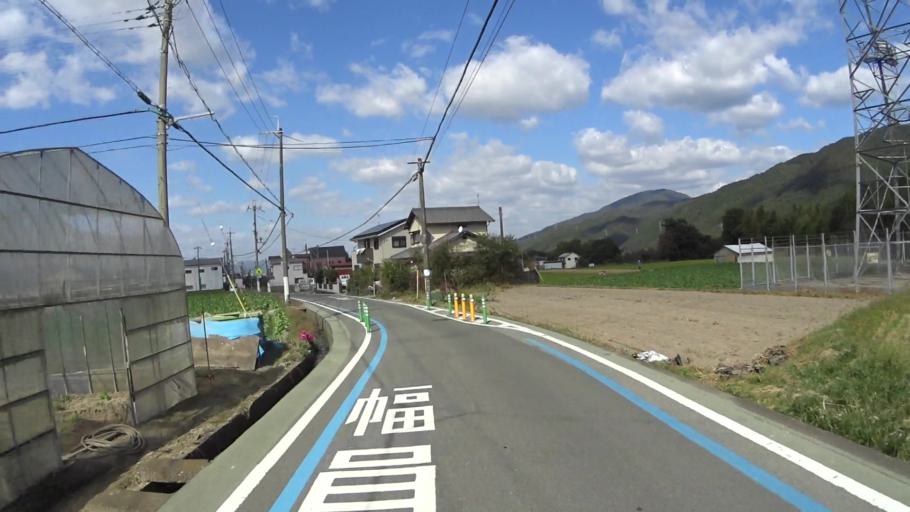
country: JP
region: Kyoto
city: Kameoka
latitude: 34.9983
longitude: 135.6158
